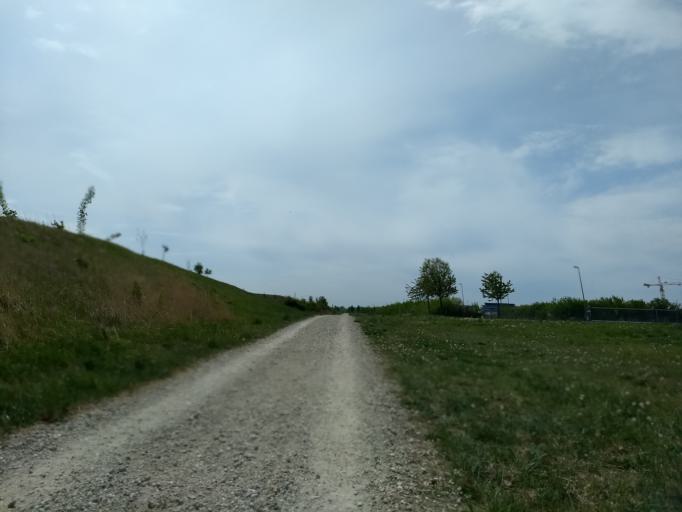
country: AT
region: Lower Austria
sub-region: Politischer Bezirk Ganserndorf
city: Gross-Enzersdorf
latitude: 48.2300
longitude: 16.5160
